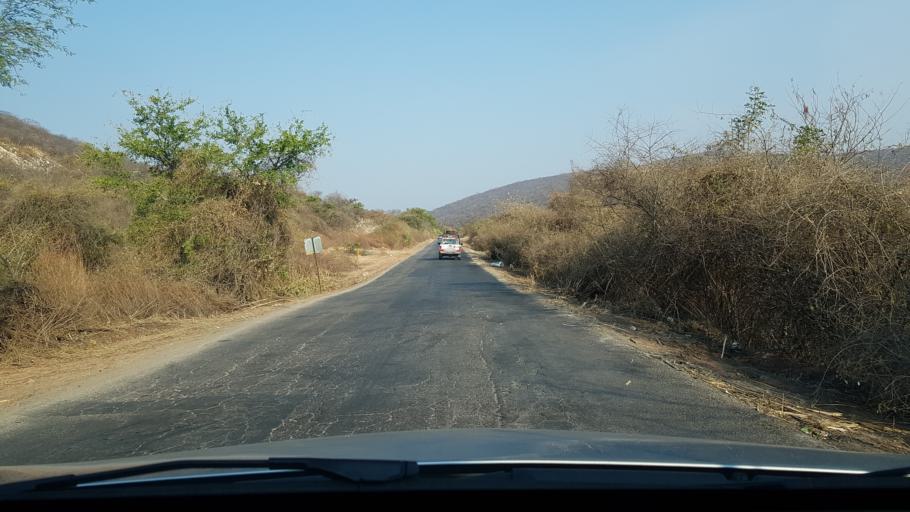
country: MX
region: Morelos
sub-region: Tlaltizapan de Zapata
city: Colonia Palo Prieto (Chipitongo)
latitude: 18.6724
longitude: -99.0575
